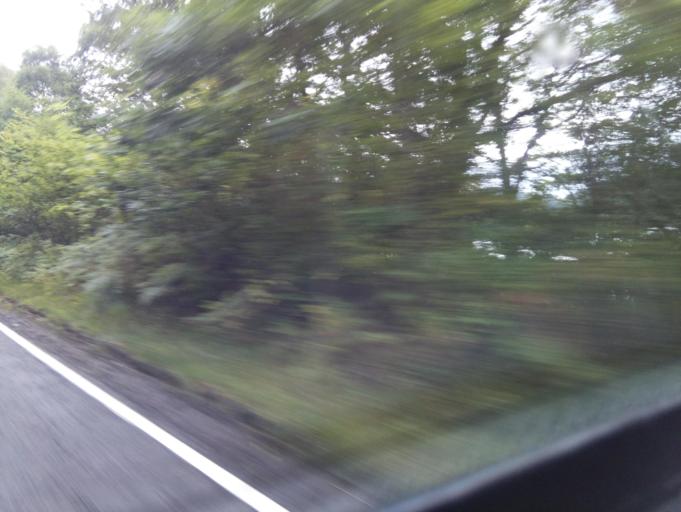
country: GB
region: Scotland
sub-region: Highland
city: Beauly
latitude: 57.2859
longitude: -4.4870
